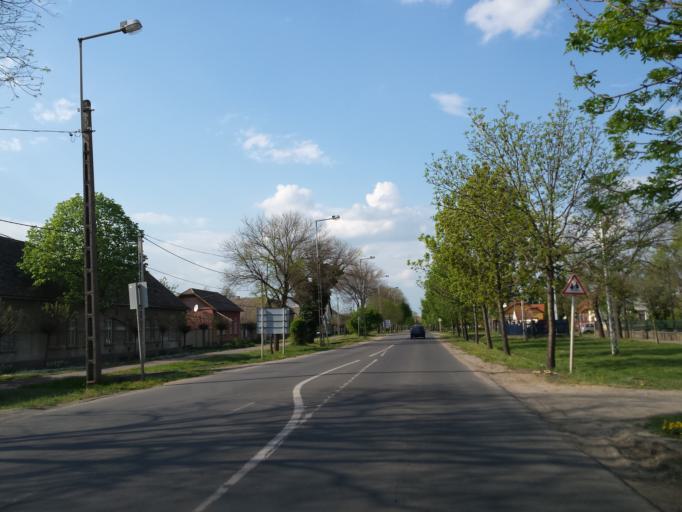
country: HU
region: Csongrad
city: Mako
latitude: 46.2299
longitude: 20.4808
